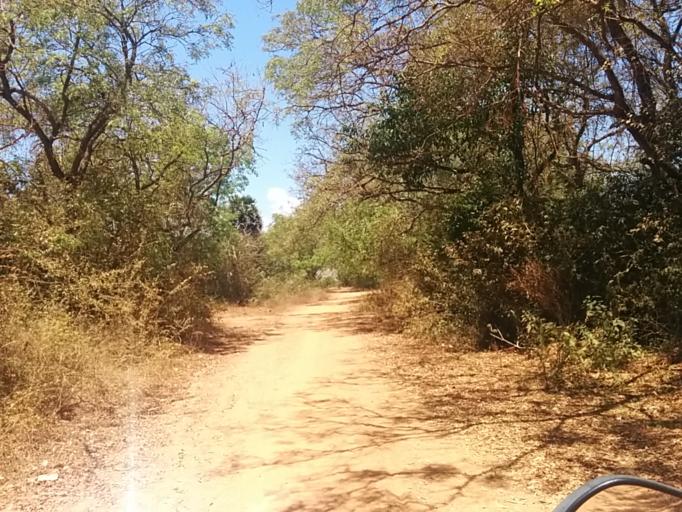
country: IN
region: Tamil Nadu
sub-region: Villupuram
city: Auroville
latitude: 12.0079
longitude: 79.8078
